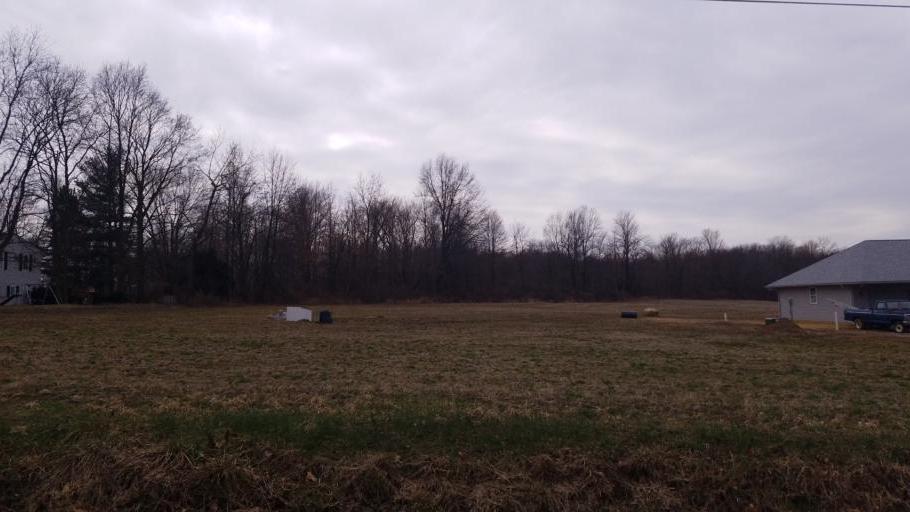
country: US
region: Ohio
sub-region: Richland County
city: Mansfield
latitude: 40.7062
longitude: -82.4760
